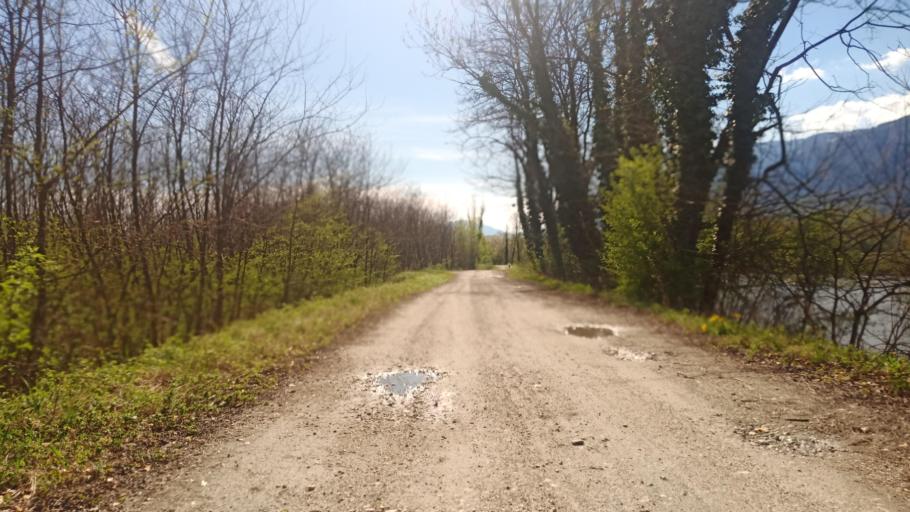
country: FR
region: Rhone-Alpes
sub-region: Departement de l'Isere
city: Froges
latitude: 45.2909
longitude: 5.9248
